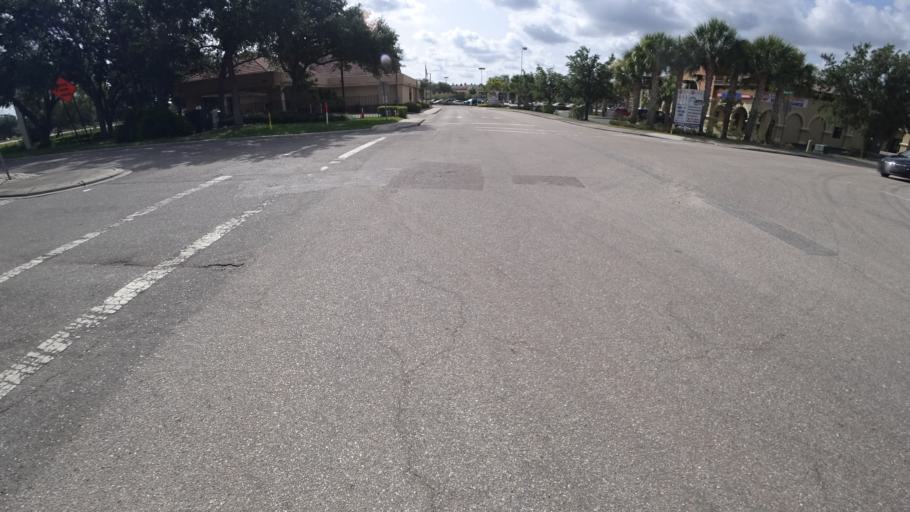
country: US
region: Florida
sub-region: Sarasota County
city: Desoto Lakes
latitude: 27.4426
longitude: -82.4669
